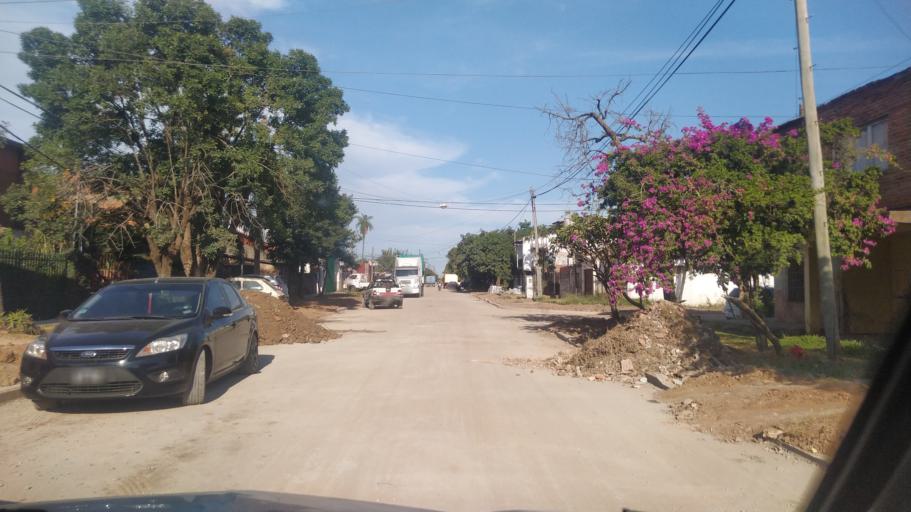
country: AR
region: Corrientes
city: Corrientes
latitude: -27.4800
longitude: -58.8125
